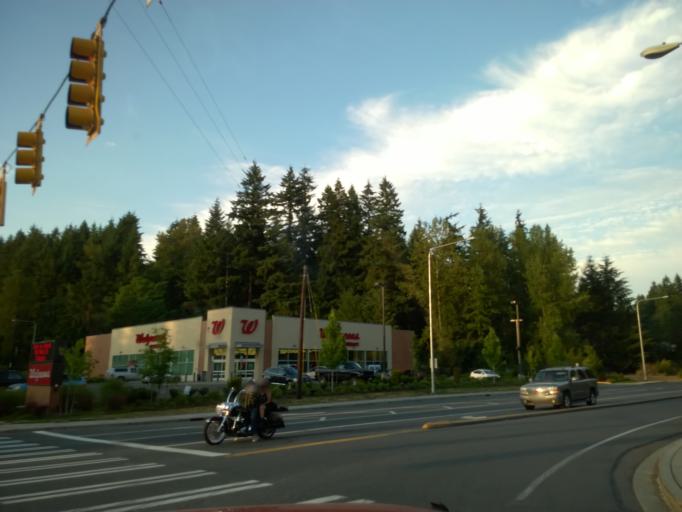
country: US
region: Washington
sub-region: King County
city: Cottage Lake
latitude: 47.7549
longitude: -122.0802
